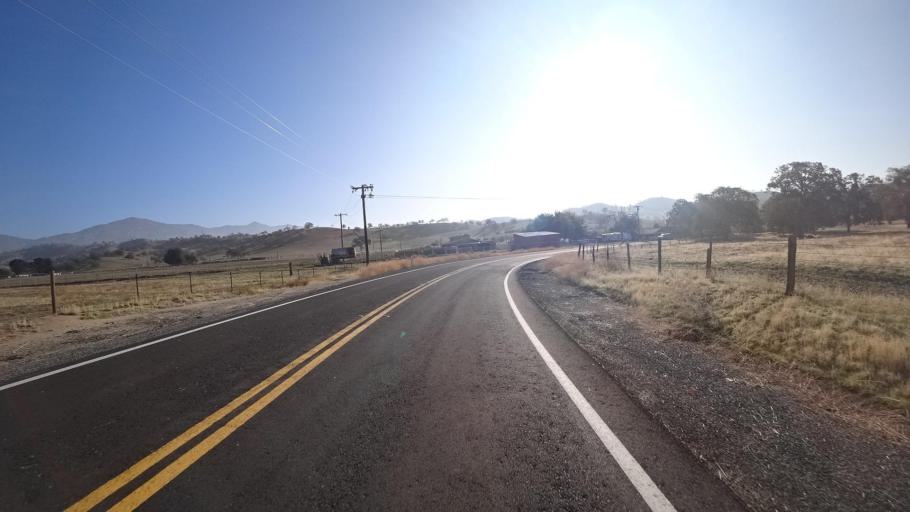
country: US
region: California
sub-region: Tulare County
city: Richgrove
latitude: 35.7373
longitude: -118.8600
